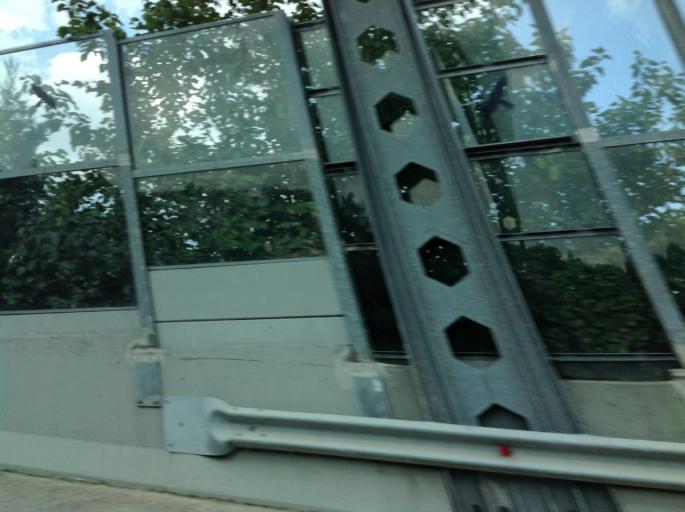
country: GR
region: Attica
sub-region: Nomarchia Anatolikis Attikis
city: Leondarion
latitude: 37.9997
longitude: 23.8444
